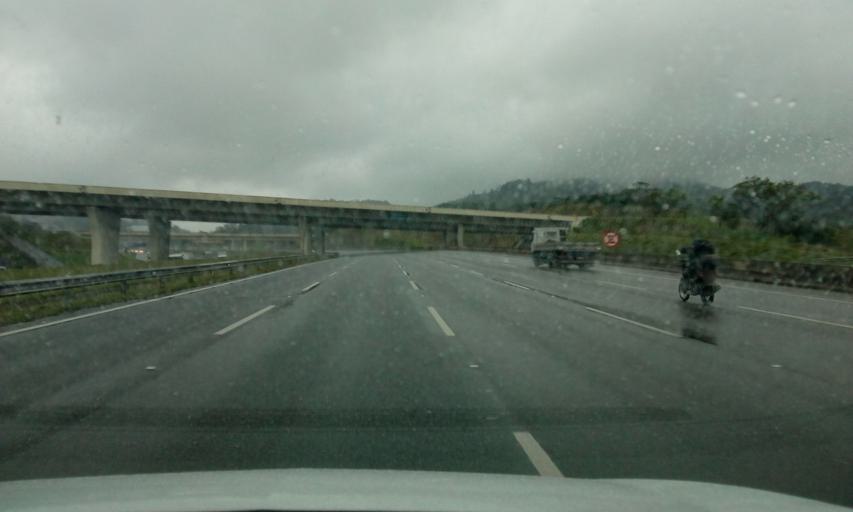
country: BR
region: Sao Paulo
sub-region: Caieiras
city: Caieiras
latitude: -23.4323
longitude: -46.7605
